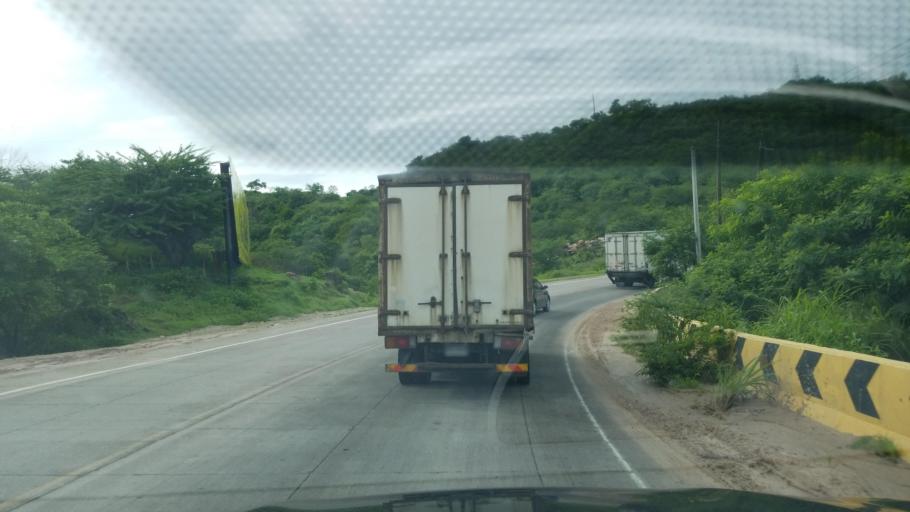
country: HN
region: Francisco Morazan
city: El Porvenir
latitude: 13.6794
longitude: -87.3535
